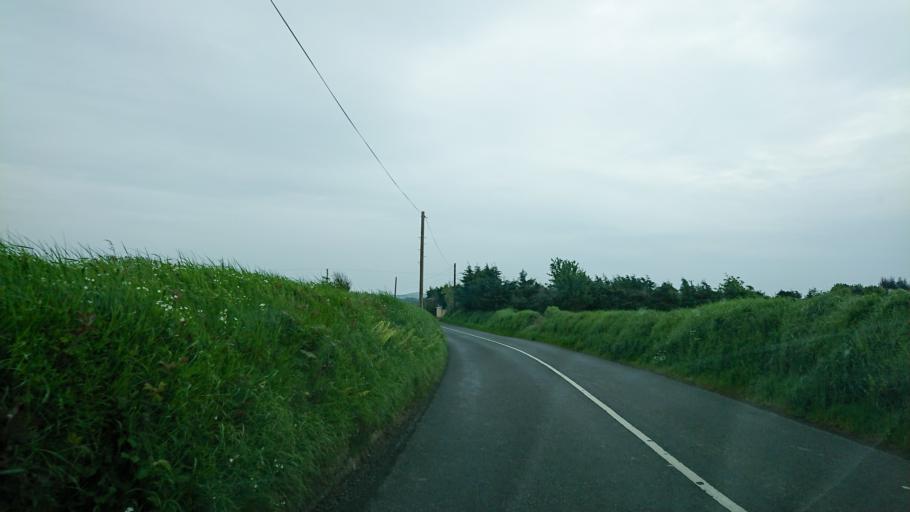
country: IE
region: Munster
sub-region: Waterford
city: Waterford
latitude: 52.2225
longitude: -7.0526
